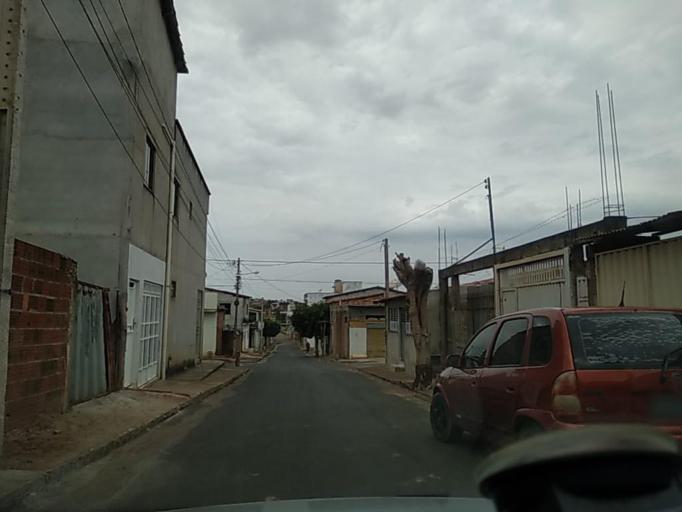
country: BR
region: Bahia
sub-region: Caetite
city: Caetite
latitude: -14.0591
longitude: -42.4816
